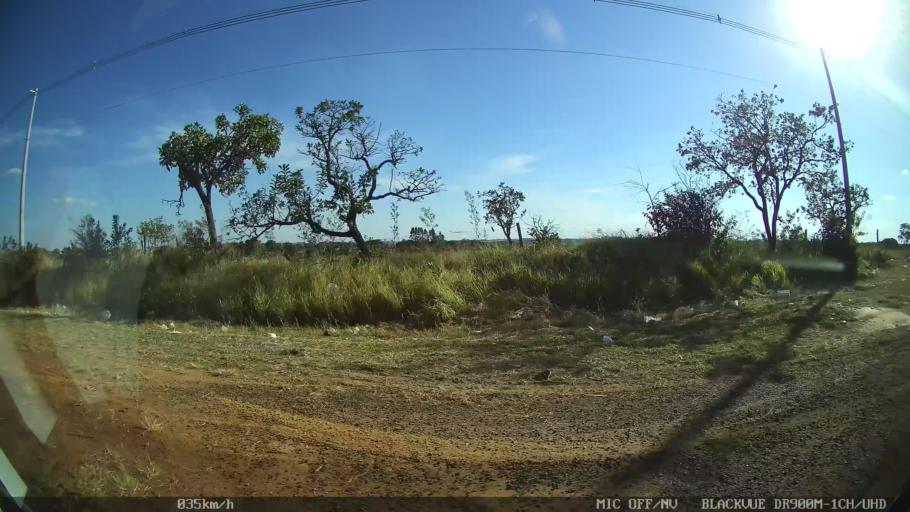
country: BR
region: Sao Paulo
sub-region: Franca
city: Franca
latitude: -20.5070
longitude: -47.4414
